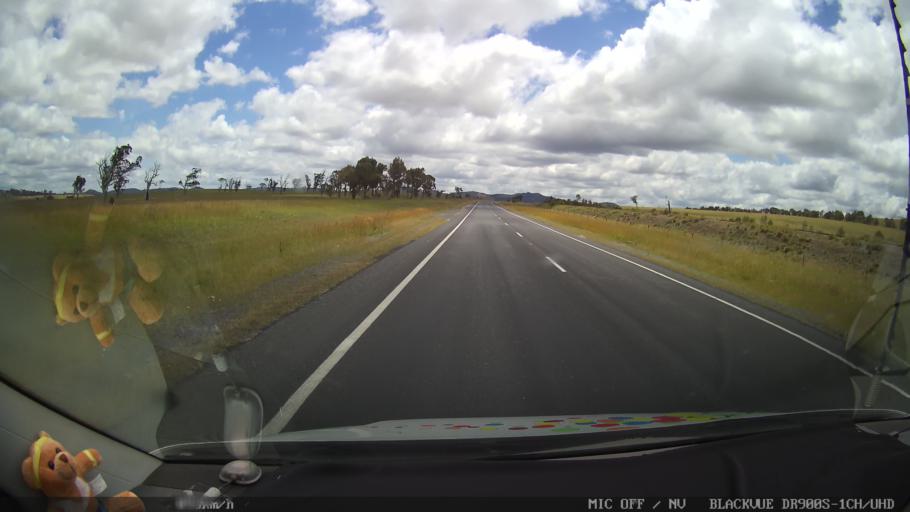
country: AU
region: New South Wales
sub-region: Glen Innes Severn
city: Glen Innes
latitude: -29.3984
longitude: 151.8761
